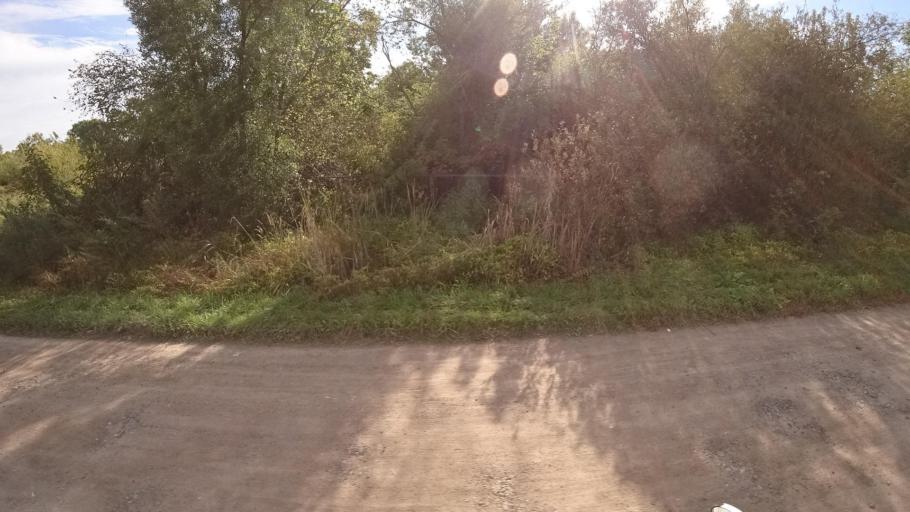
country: RU
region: Primorskiy
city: Dostoyevka
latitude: 44.3028
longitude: 133.4571
